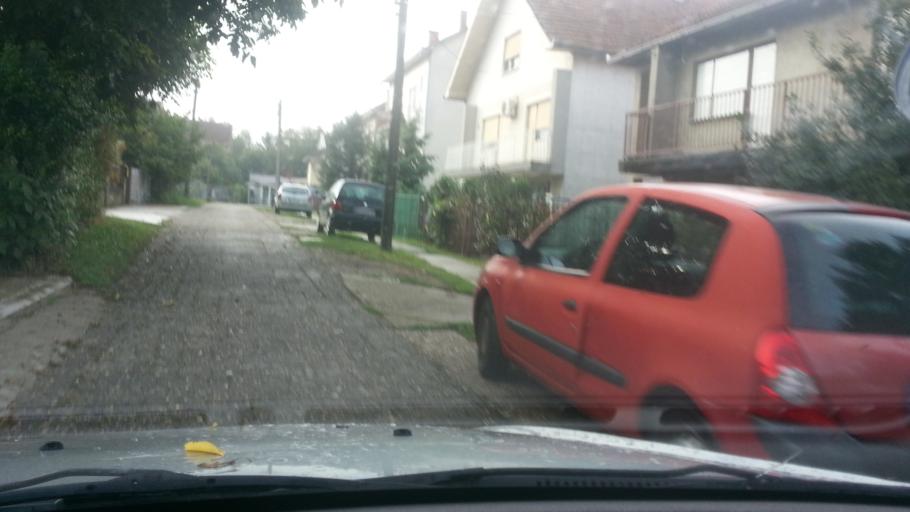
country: RS
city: Novi Banovci
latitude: 44.9469
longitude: 20.2892
